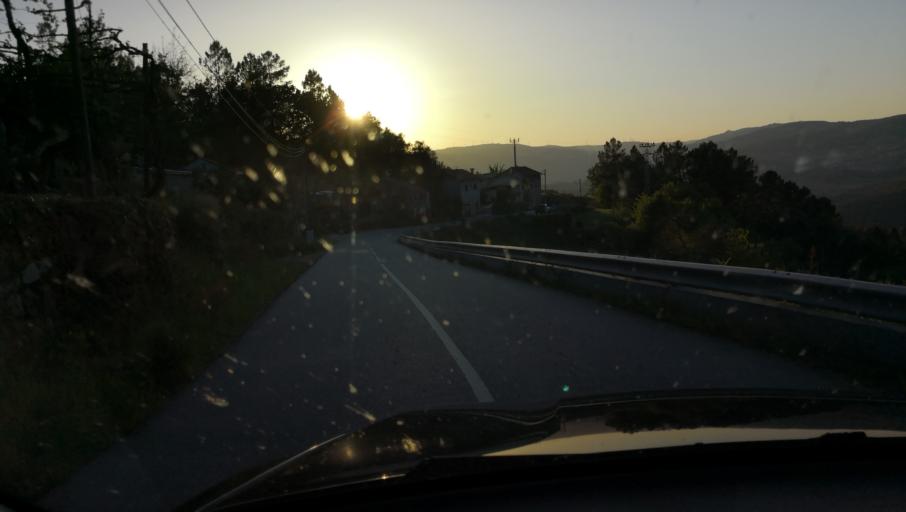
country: PT
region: Vila Real
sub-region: Mondim de Basto
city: Mondim de Basto
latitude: 41.4104
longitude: -7.9320
